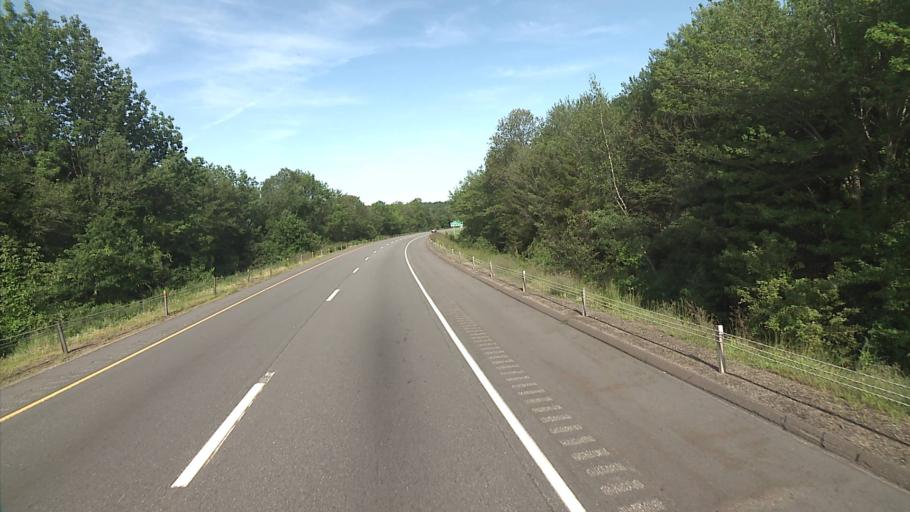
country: US
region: Connecticut
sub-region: New London County
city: Colchester
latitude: 41.5627
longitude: -72.3209
